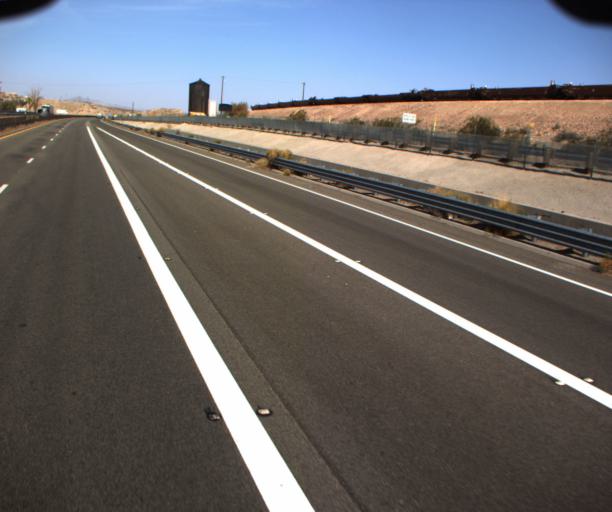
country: US
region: California
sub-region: San Bernardino County
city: Needles
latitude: 34.7178
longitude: -114.4809
